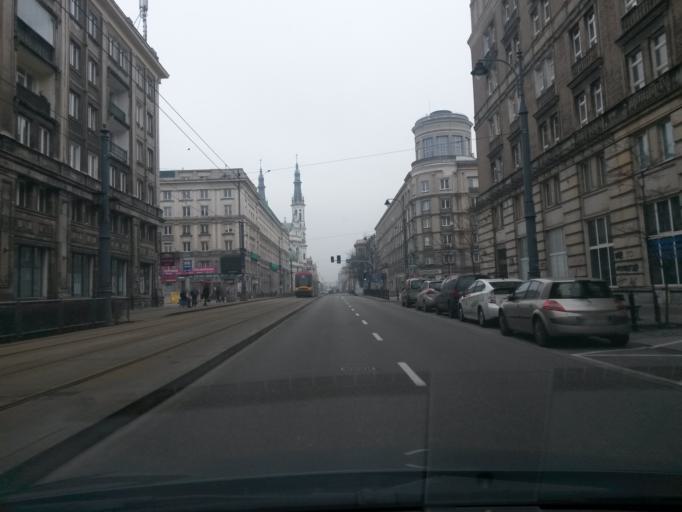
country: PL
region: Masovian Voivodeship
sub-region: Warszawa
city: Srodmiescie
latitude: 52.2173
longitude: 21.0195
